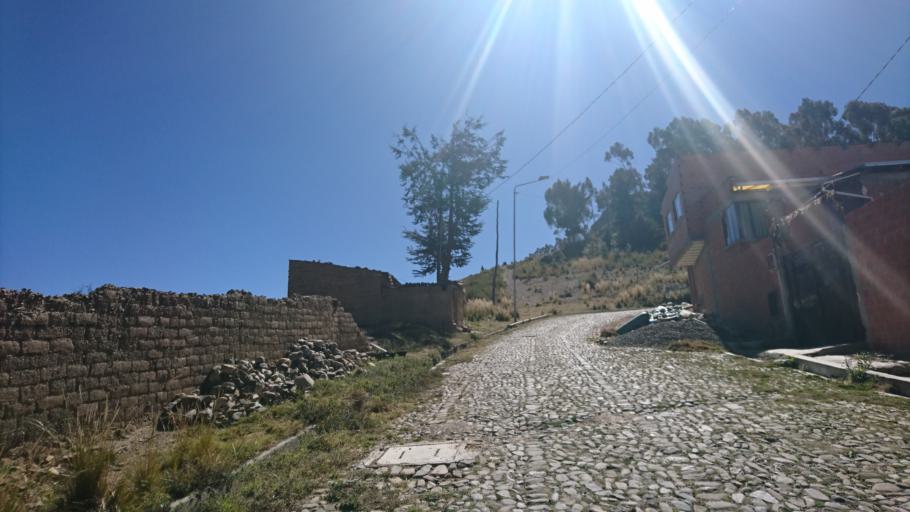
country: BO
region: La Paz
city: La Paz
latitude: -16.4871
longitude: -68.1049
